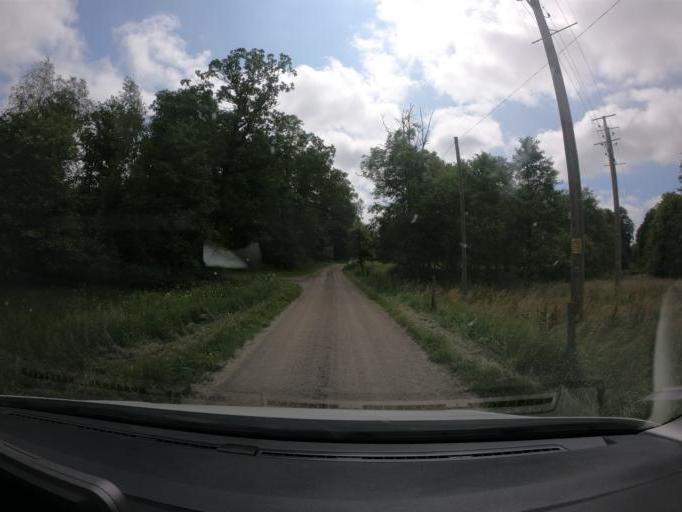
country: SE
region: Skane
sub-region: Hassleholms Kommun
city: Sosdala
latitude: 56.0504
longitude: 13.5712
